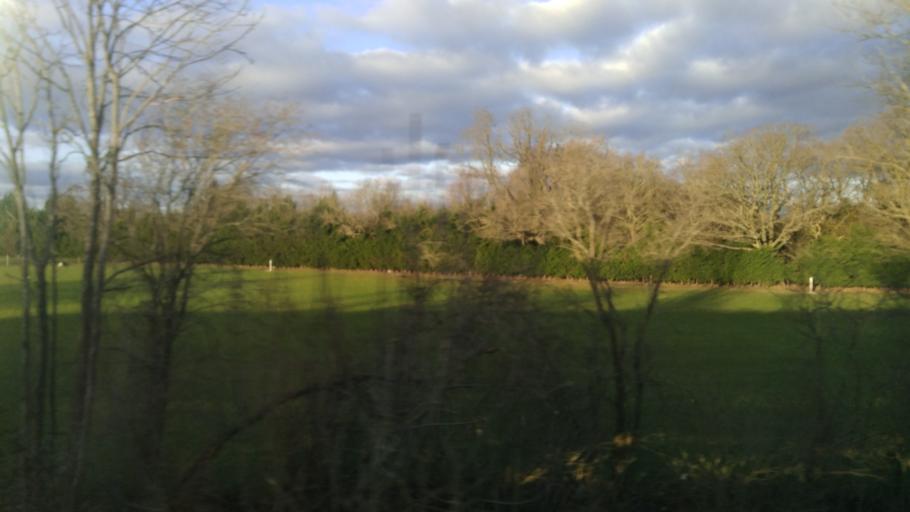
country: GB
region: England
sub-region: Kent
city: Headcorn
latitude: 51.1630
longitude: 0.6631
